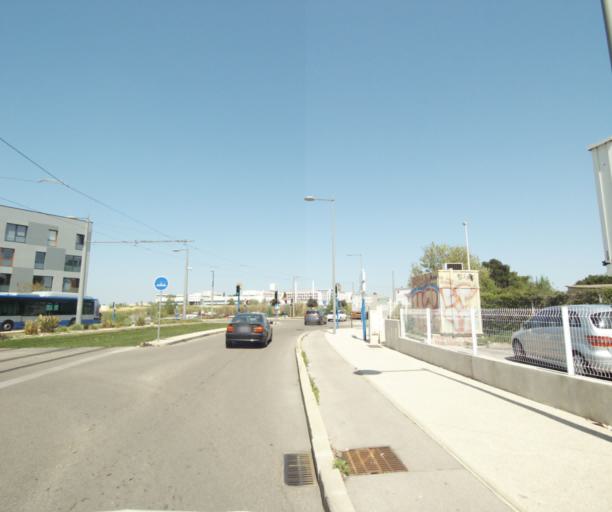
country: FR
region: Languedoc-Roussillon
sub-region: Departement de l'Herault
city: Juvignac
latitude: 43.6168
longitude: 3.8260
